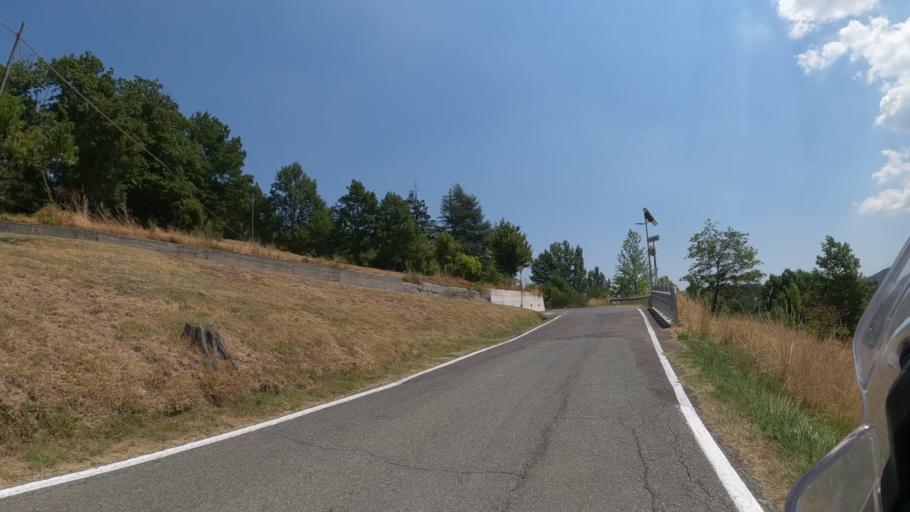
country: IT
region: Piedmont
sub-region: Provincia di Alessandria
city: Cassinelle-Concentrico
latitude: 44.5789
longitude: 8.5474
